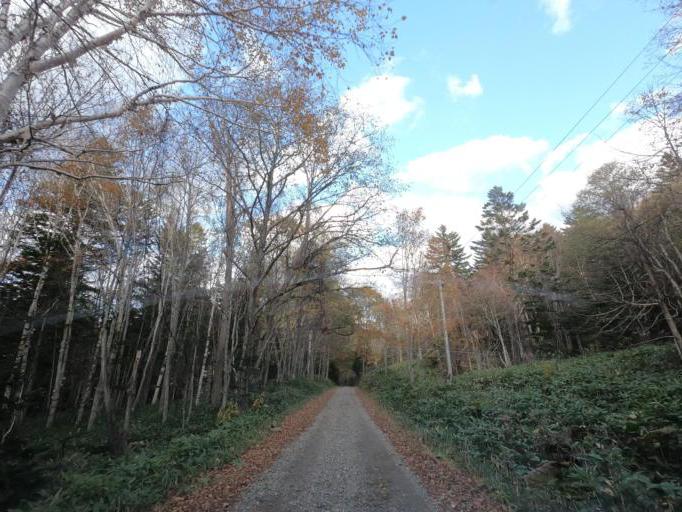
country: JP
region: Hokkaido
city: Otofuke
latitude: 43.4314
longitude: 143.1474
